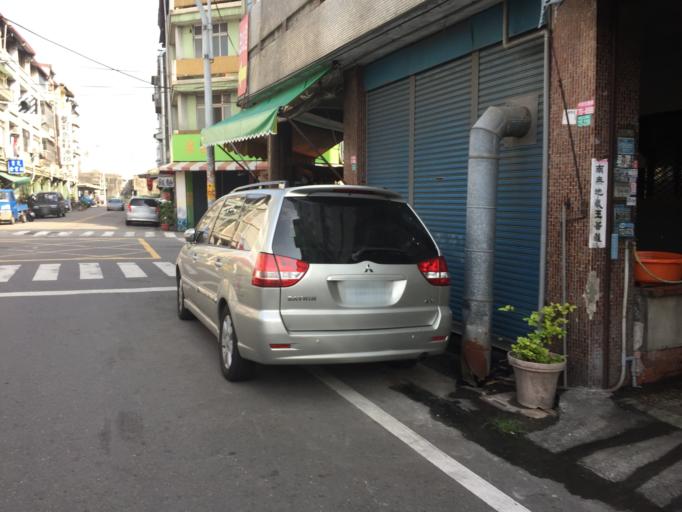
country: TW
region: Taiwan
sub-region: Changhua
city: Chang-hua
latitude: 24.0848
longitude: 120.5502
